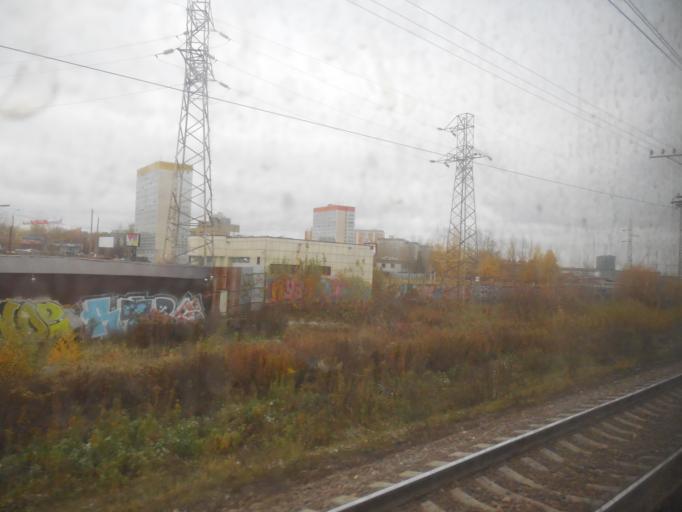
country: RU
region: Moskovskaya
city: Odintsovo
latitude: 55.6679
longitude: 37.2608
